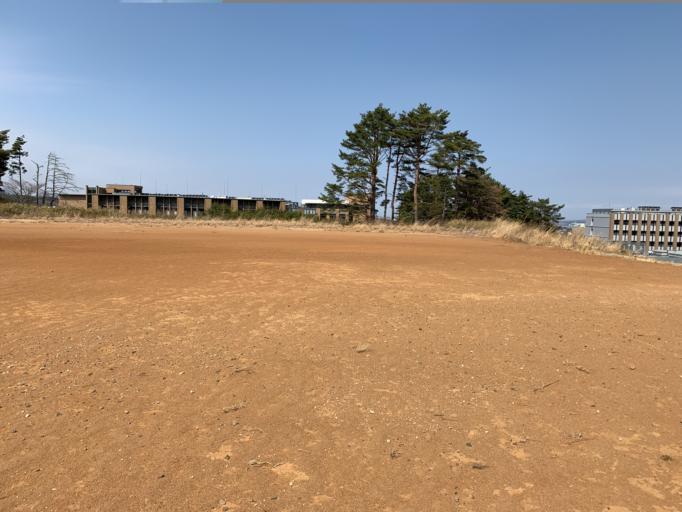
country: JP
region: Miyagi
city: Sendai
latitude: 38.2537
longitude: 140.8305
